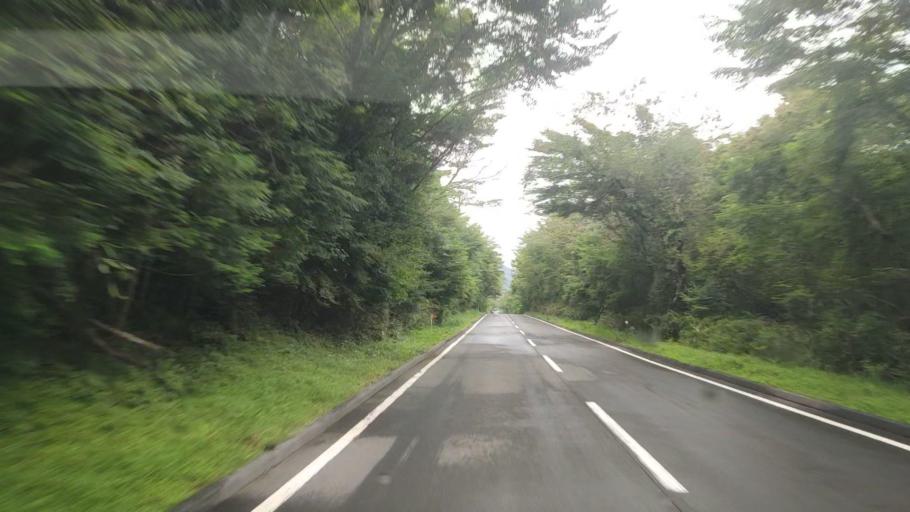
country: JP
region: Shizuoka
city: Gotemba
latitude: 35.2735
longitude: 138.7969
